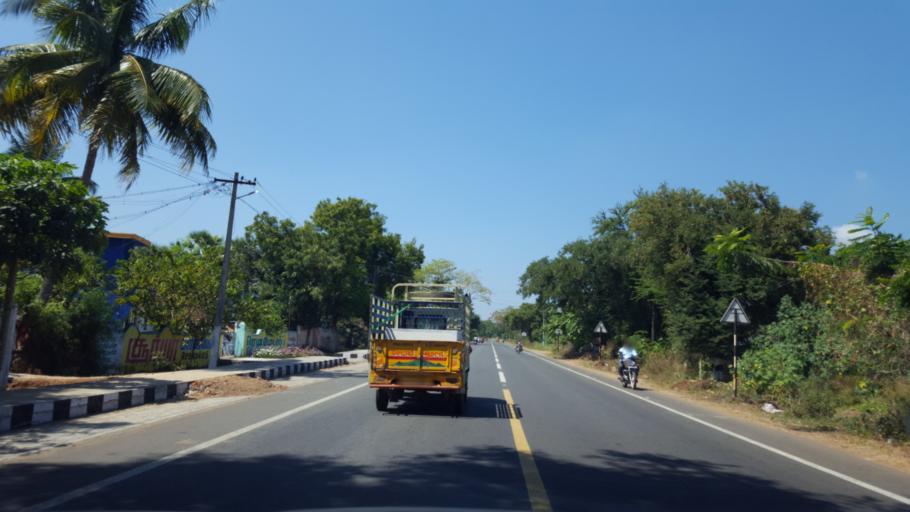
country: IN
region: Tamil Nadu
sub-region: Kancheepuram
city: Karumbakkam
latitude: 12.6436
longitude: 80.0412
